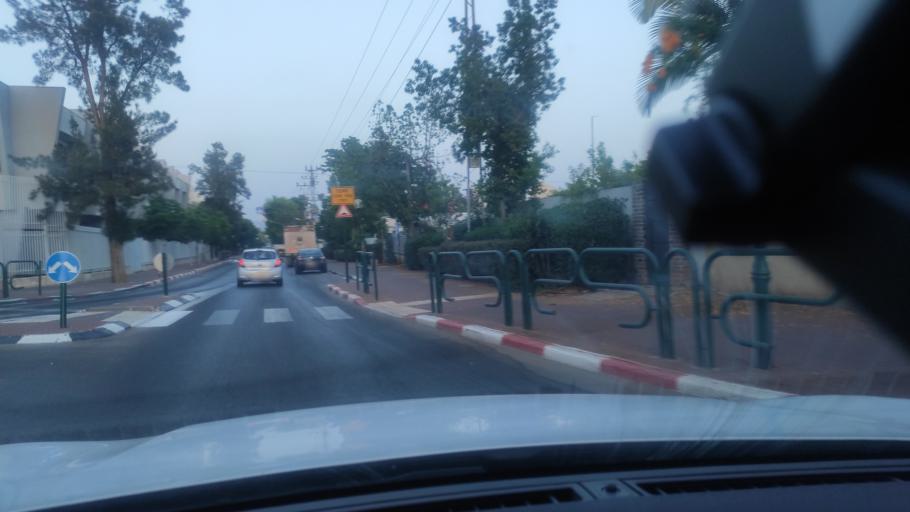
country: IL
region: Central District
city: Kfar Saba
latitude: 32.1832
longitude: 34.9126
